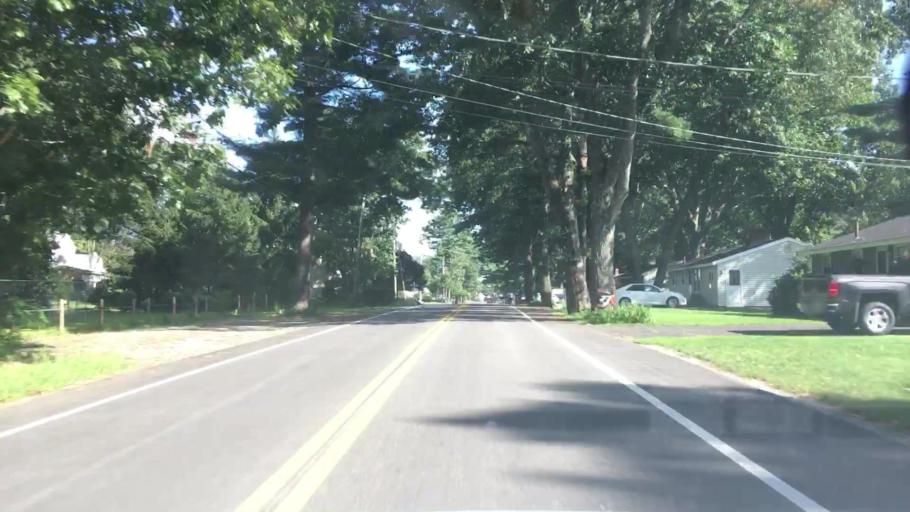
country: US
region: New Hampshire
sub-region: Strafford County
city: Dover
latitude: 43.1619
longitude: -70.8779
